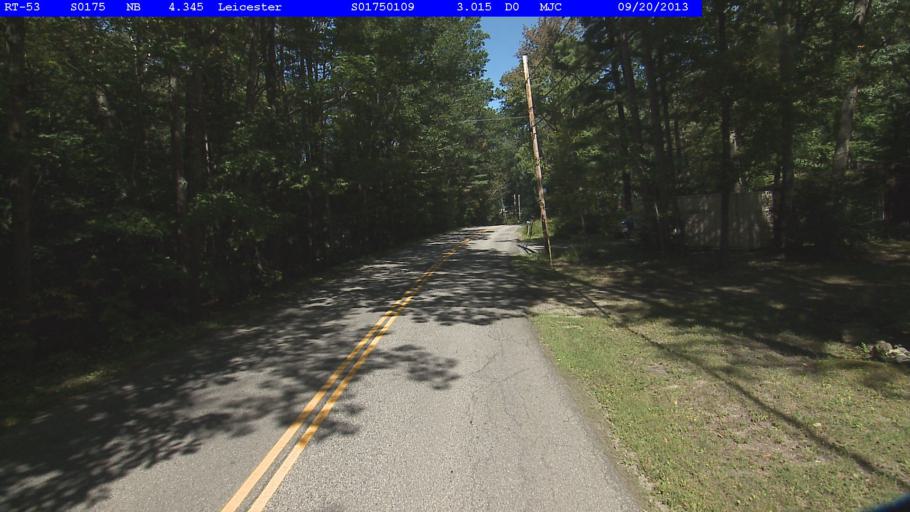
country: US
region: Vermont
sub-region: Rutland County
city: Brandon
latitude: 43.8860
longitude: -73.0644
